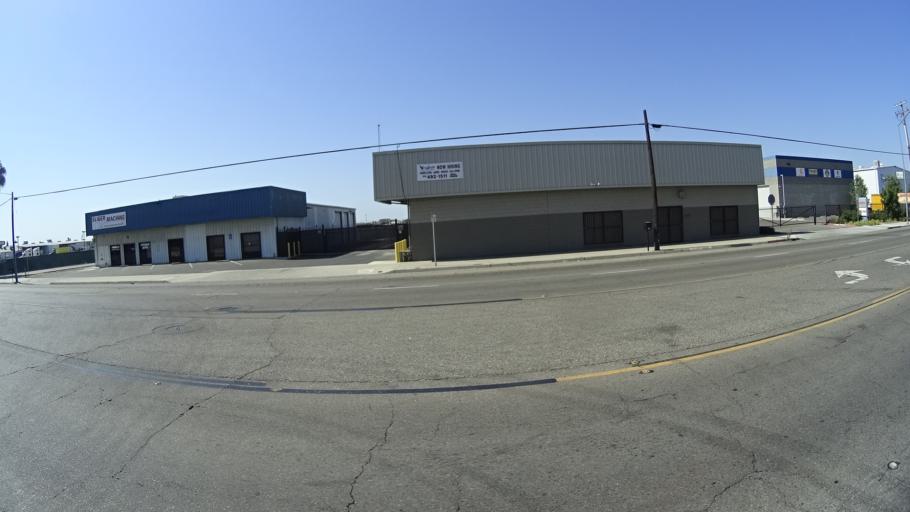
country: US
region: California
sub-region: Fresno County
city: Fresno
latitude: 36.7071
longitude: -119.7789
